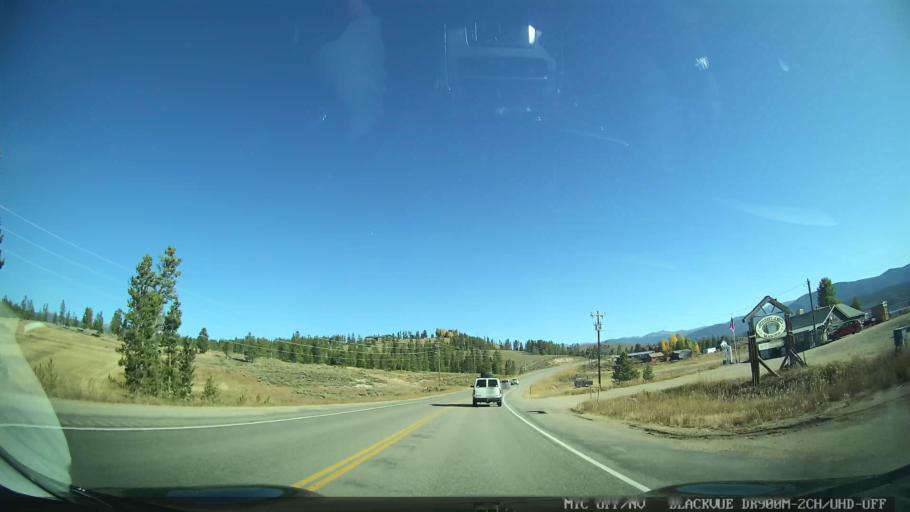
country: US
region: Colorado
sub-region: Grand County
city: Granby
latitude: 40.1732
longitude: -105.9008
